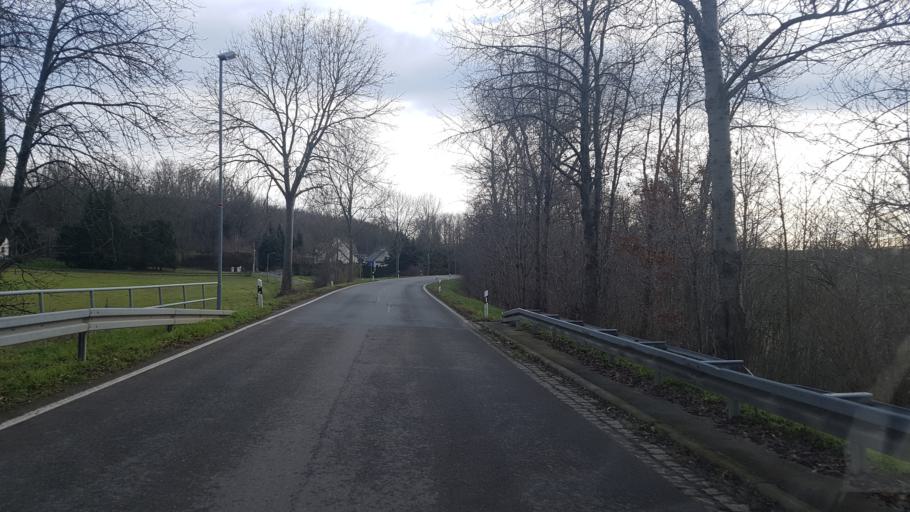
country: DE
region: Saxony
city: Ostrau
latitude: 51.1973
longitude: 13.1640
